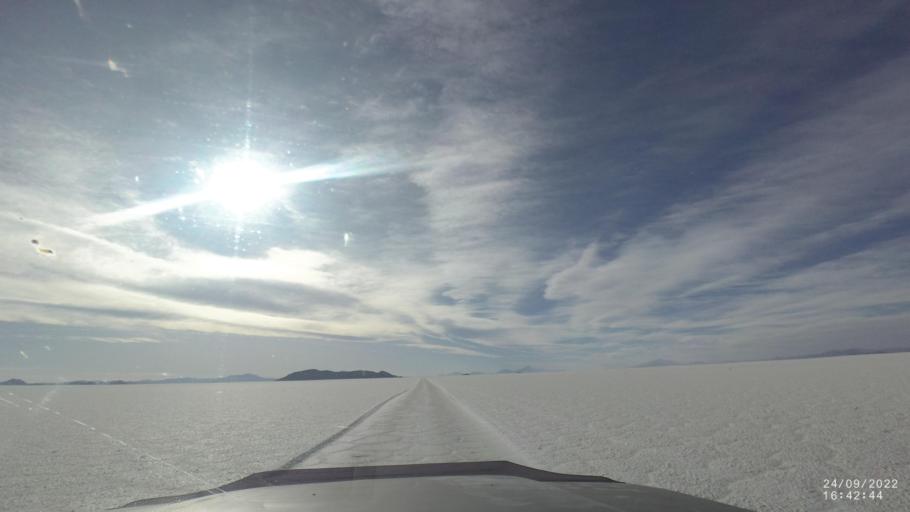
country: BO
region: Potosi
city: Colchani
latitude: -20.1723
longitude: -67.7364
